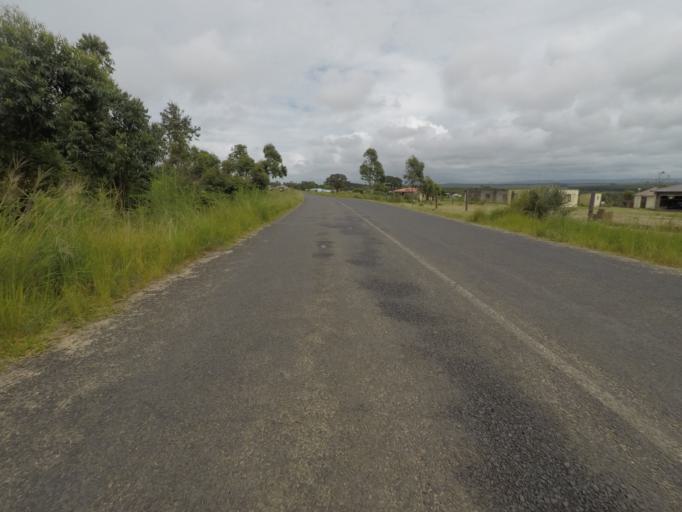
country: ZA
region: KwaZulu-Natal
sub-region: uThungulu District Municipality
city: eSikhawini
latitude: -28.9132
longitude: 31.8537
